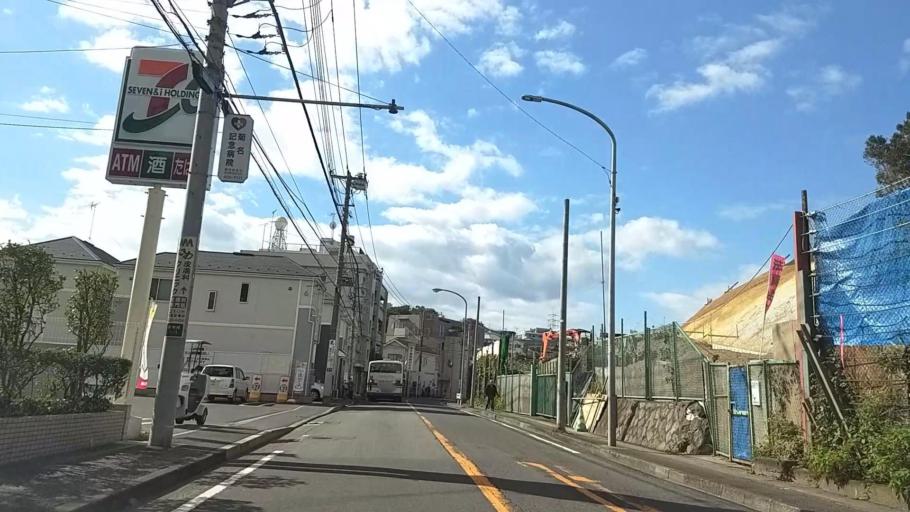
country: JP
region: Kanagawa
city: Yokohama
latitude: 35.5035
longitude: 139.6443
